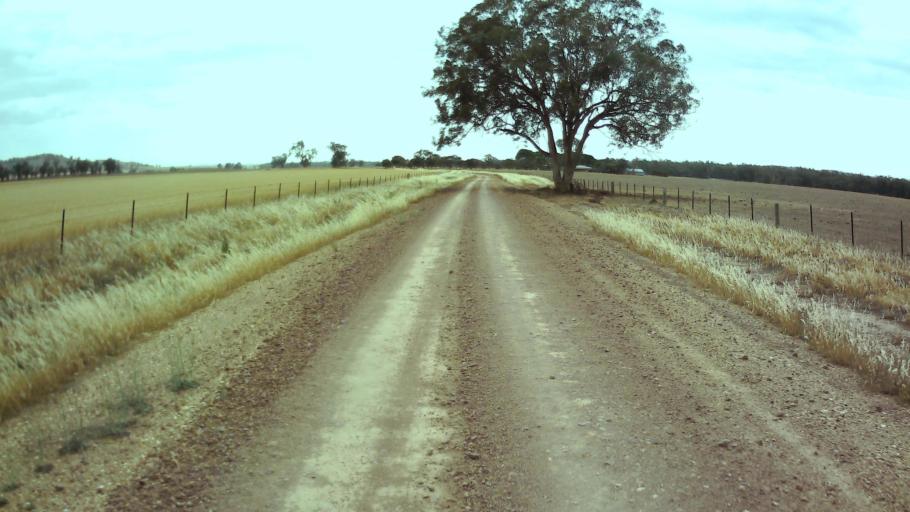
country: AU
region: New South Wales
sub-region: Weddin
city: Grenfell
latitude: -33.9185
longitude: 148.2868
